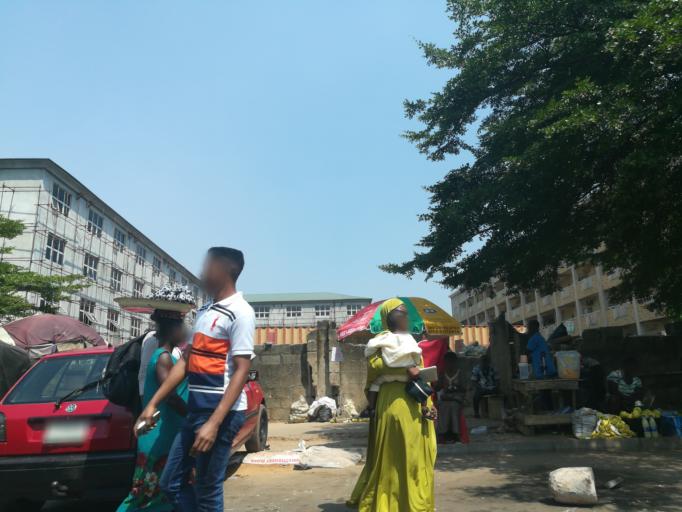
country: NG
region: Abuja Federal Capital Territory
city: Abuja
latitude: 9.0668
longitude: 7.4455
